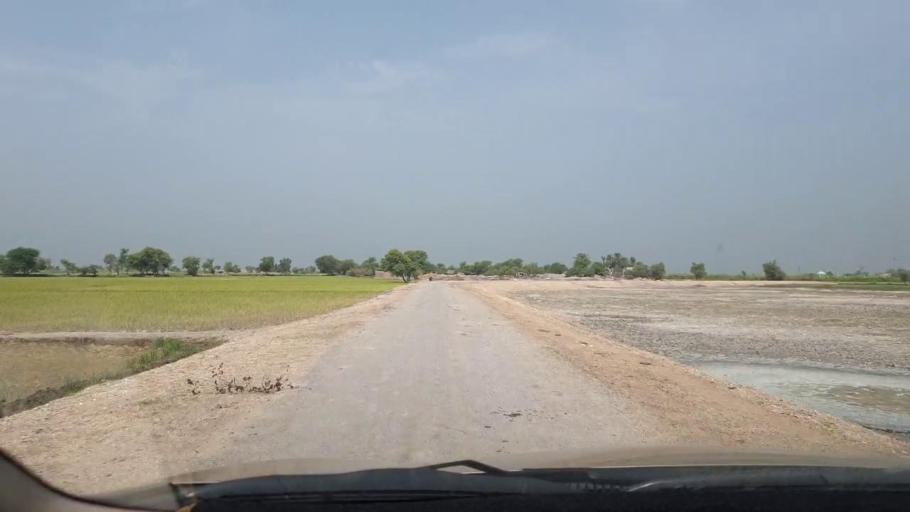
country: PK
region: Sindh
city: Goth Garelo
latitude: 27.5241
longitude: 68.0726
